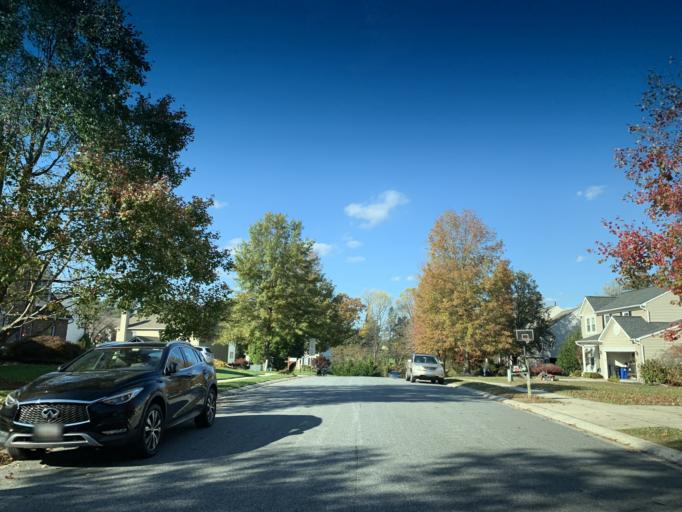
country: US
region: Maryland
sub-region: Harford County
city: Bel Air South
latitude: 39.5115
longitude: -76.3135
